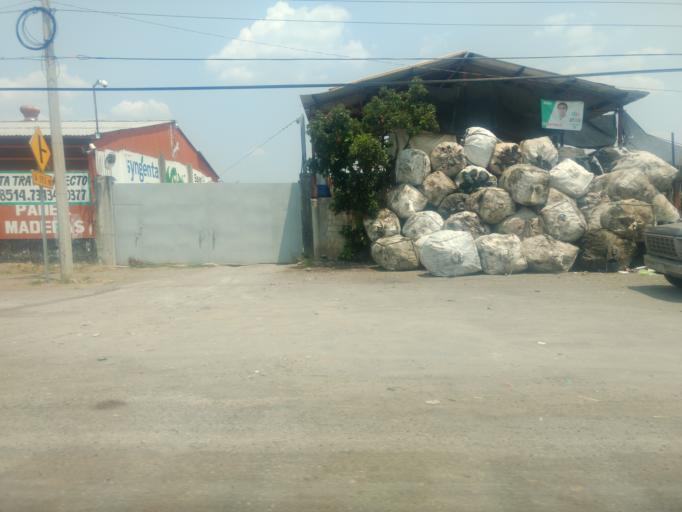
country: MX
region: Morelos
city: Puente de Ixtla
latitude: 18.6326
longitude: -99.3217
